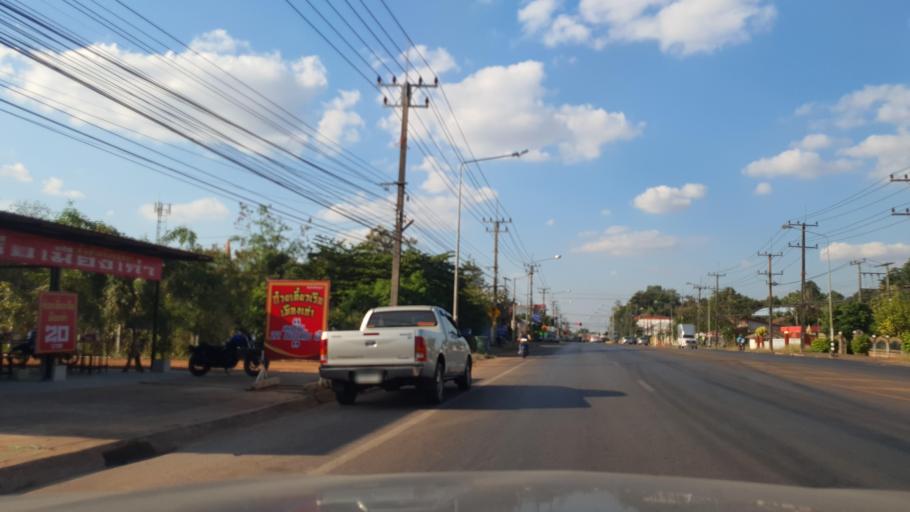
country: TH
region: Sakon Nakhon
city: Sakon Nakhon
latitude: 17.1813
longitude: 104.0948
